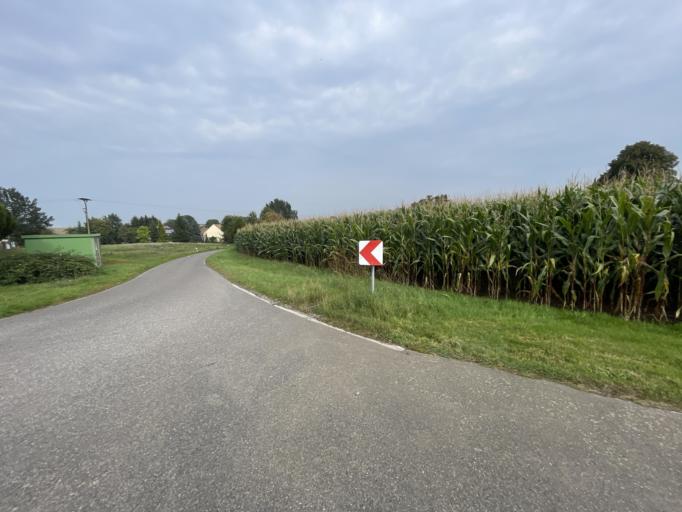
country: DE
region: Saxony
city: Claussnitz
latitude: 50.9755
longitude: 12.8660
